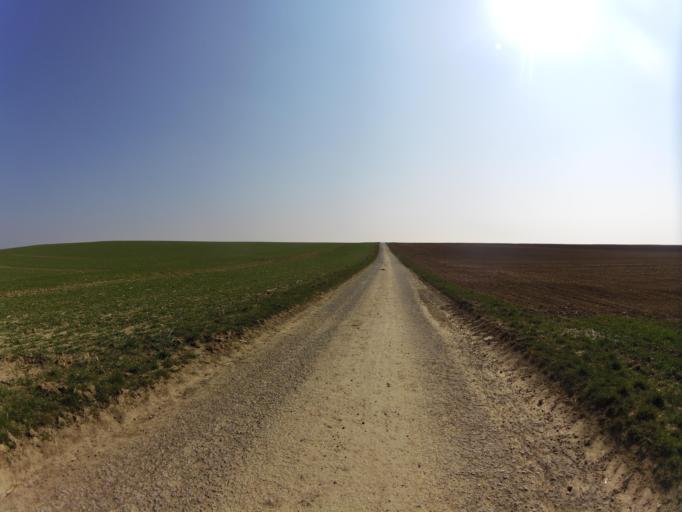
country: DE
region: Bavaria
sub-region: Regierungsbezirk Unterfranken
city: Winterhausen
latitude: 49.6855
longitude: 9.9861
